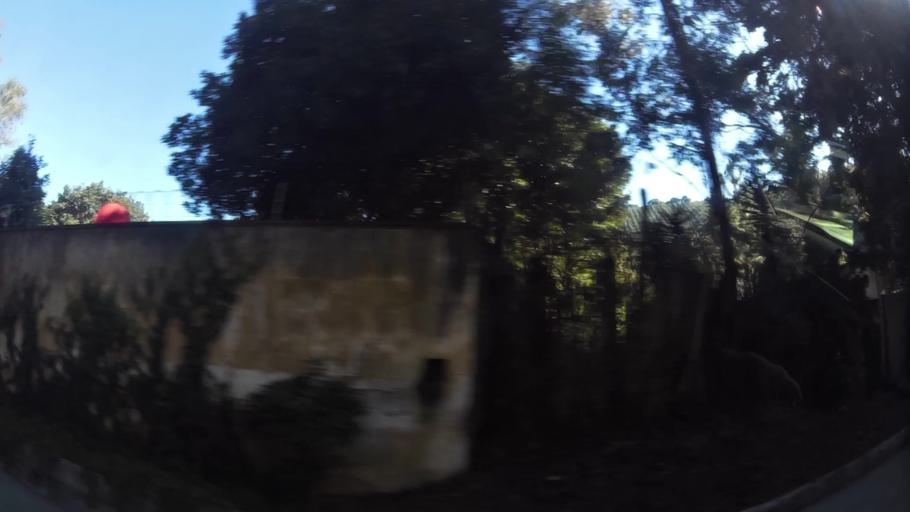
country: GT
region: Sacatepequez
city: Antigua Guatemala
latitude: 14.5611
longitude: -90.7052
